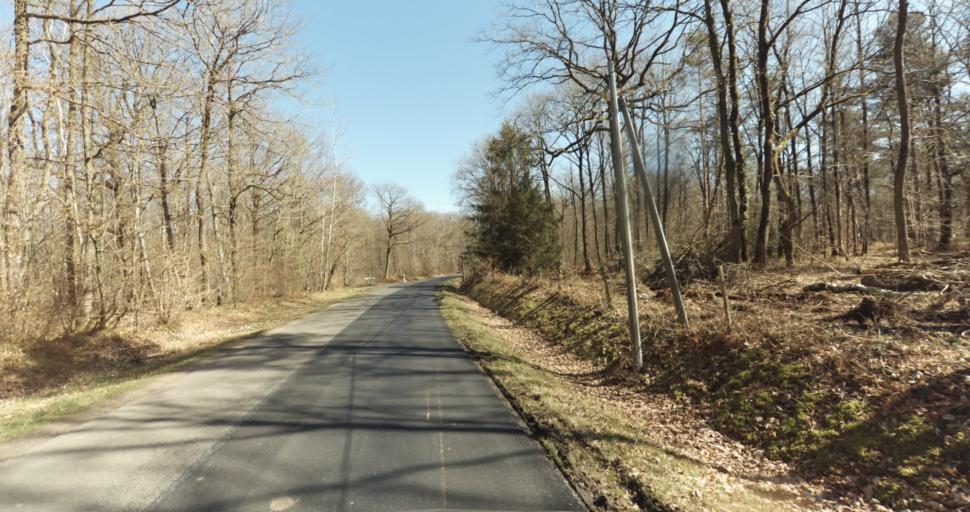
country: FR
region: Lower Normandy
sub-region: Departement de l'Orne
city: Trun
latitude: 48.9330
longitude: 0.0725
